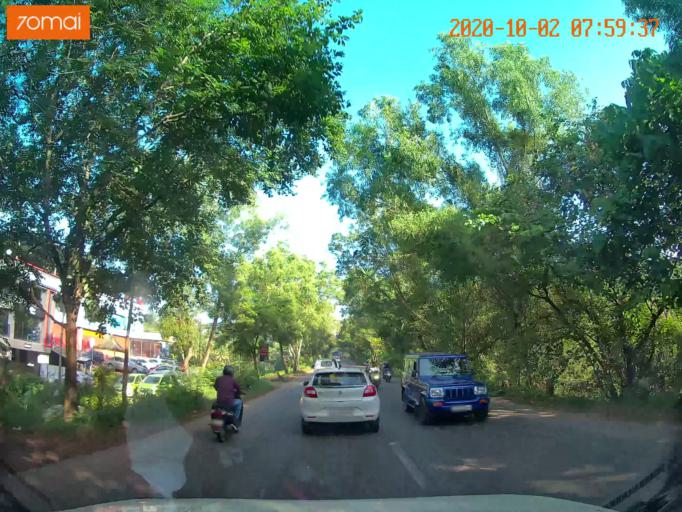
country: IN
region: Kerala
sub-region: Kozhikode
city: Ferokh
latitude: 11.2115
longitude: 75.8607
